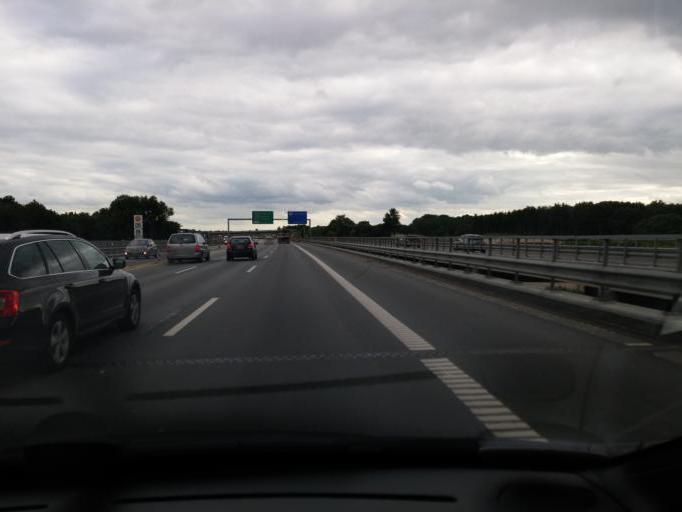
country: DK
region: Zealand
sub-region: Solrod Kommune
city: Solrod Strand
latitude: 55.5589
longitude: 12.2285
